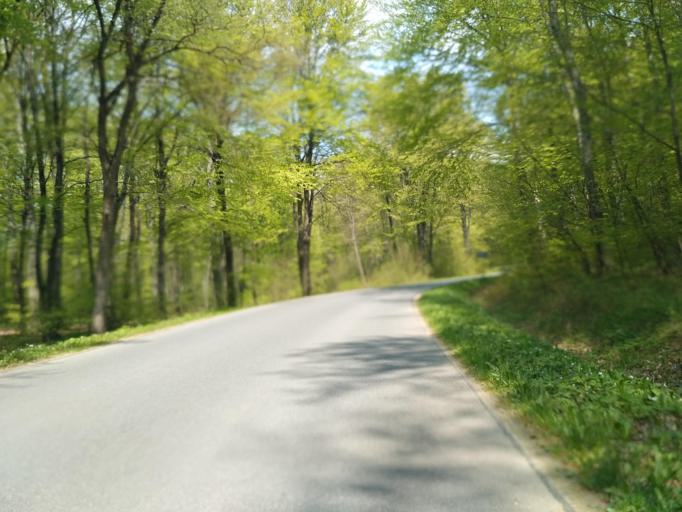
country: PL
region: Subcarpathian Voivodeship
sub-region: Powiat jasielski
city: Debowiec
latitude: 49.7034
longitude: 21.5112
